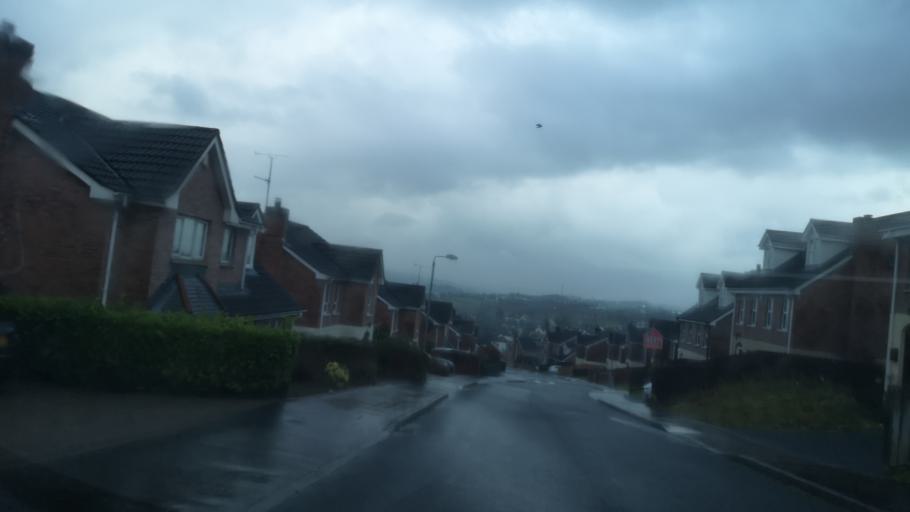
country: GB
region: Northern Ireland
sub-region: Newry and Mourne District
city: Newry
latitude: 54.1806
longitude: -6.3229
